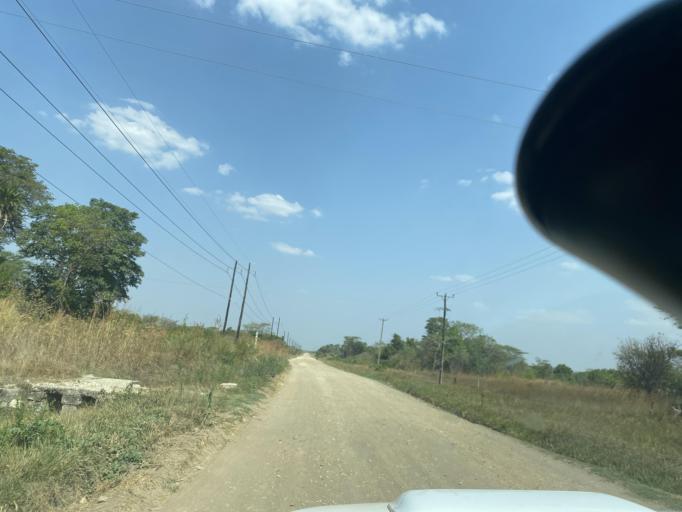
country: ZM
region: Lusaka
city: Lusaka
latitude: -15.3068
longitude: 28.0408
